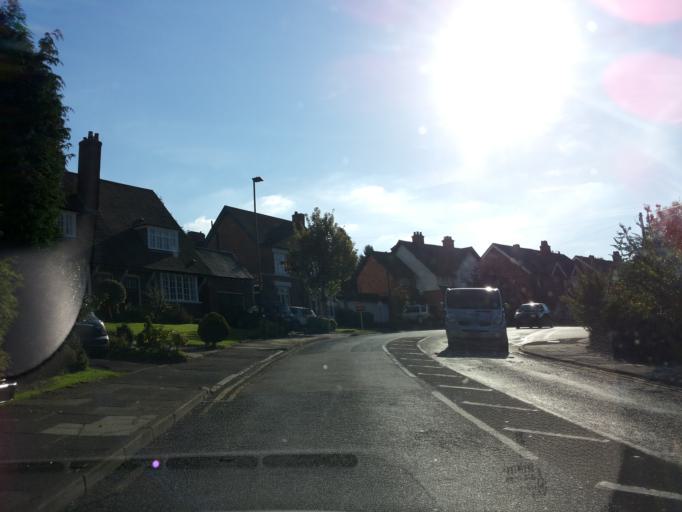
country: GB
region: England
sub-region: City and Borough of Birmingham
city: Bartley Green
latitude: 52.4254
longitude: -1.9361
